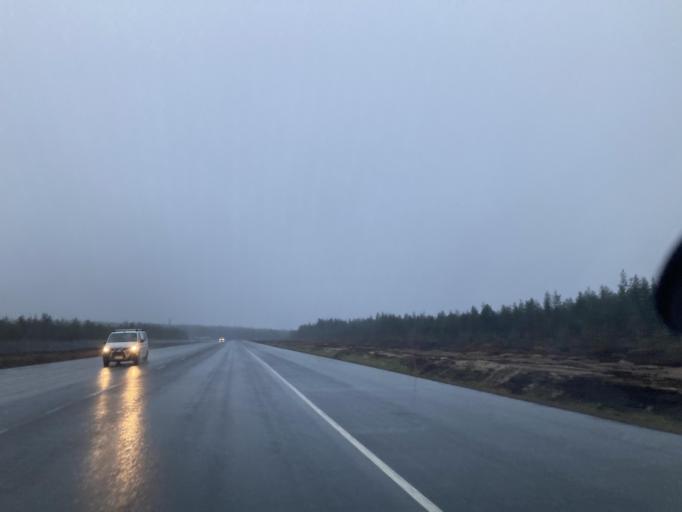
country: FI
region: Lapland
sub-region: Rovaniemi
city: Rovaniemi
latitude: 66.5665
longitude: 25.7965
